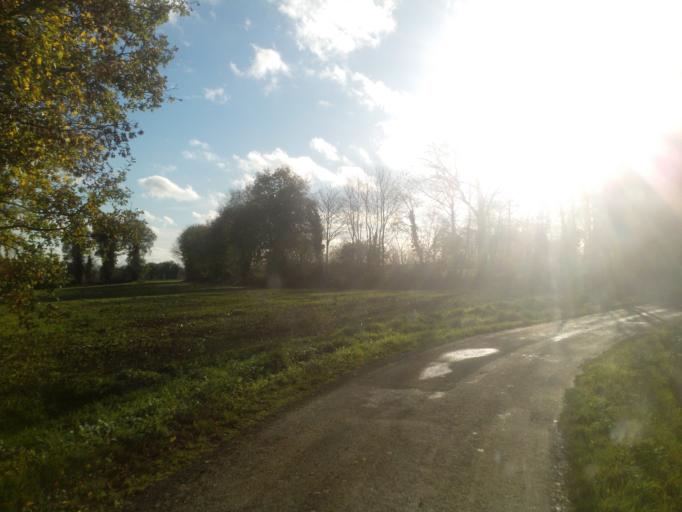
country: FR
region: Brittany
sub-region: Departement du Morbihan
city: Meneac
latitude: 48.1185
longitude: -2.4087
